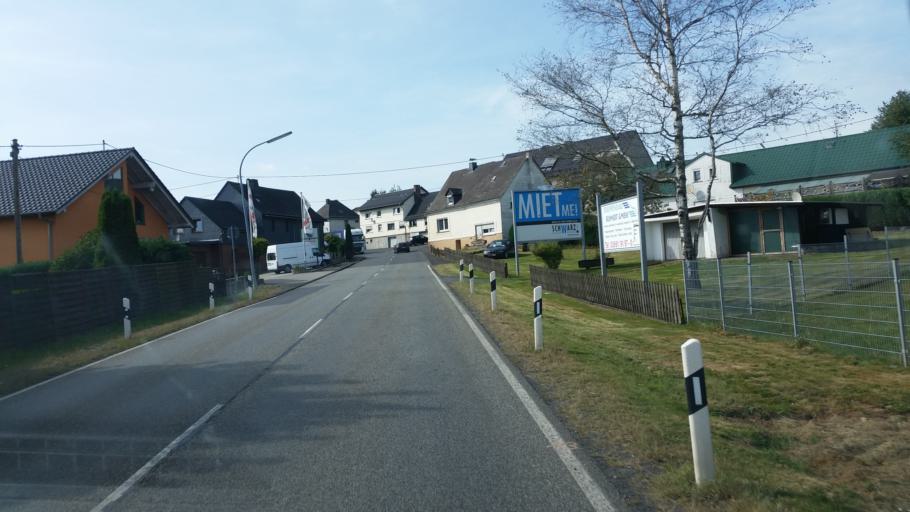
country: DE
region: Rheinland-Pfalz
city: Hohn
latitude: 50.6191
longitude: 7.9901
